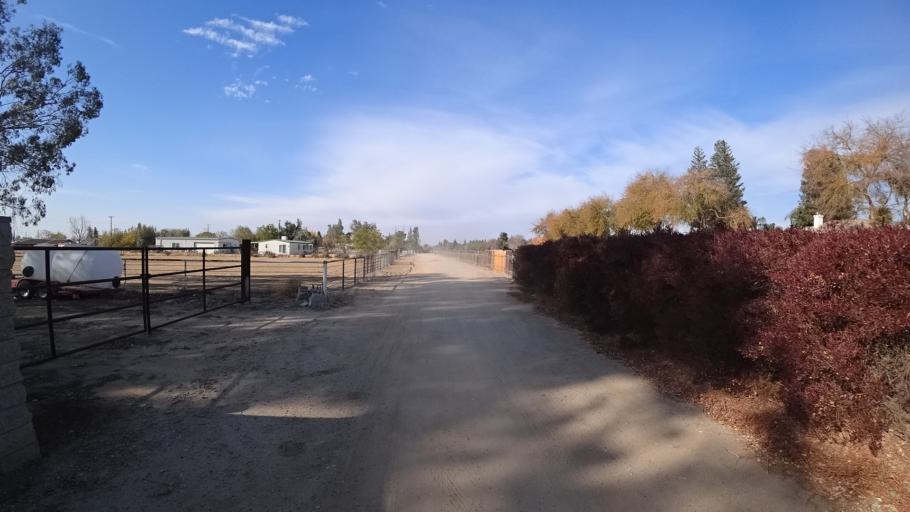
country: US
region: California
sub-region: Kern County
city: Greenacres
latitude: 35.4014
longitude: -119.0699
